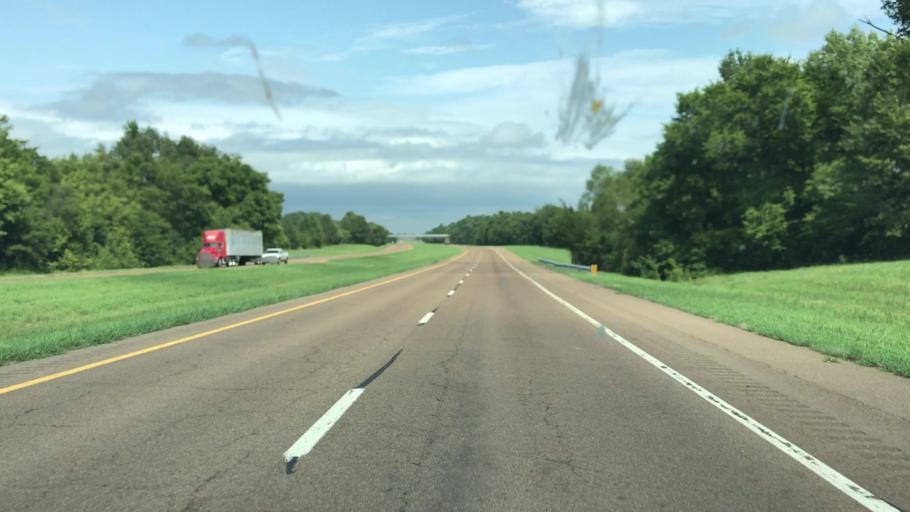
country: US
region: Tennessee
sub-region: Obion County
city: South Fulton
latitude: 36.4791
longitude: -88.9486
